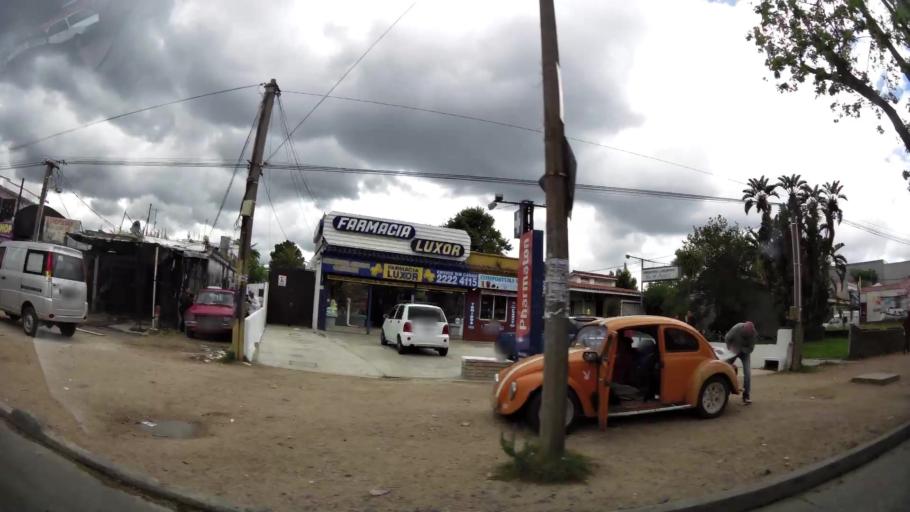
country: UY
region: Canelones
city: Toledo
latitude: -34.8174
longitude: -56.1393
